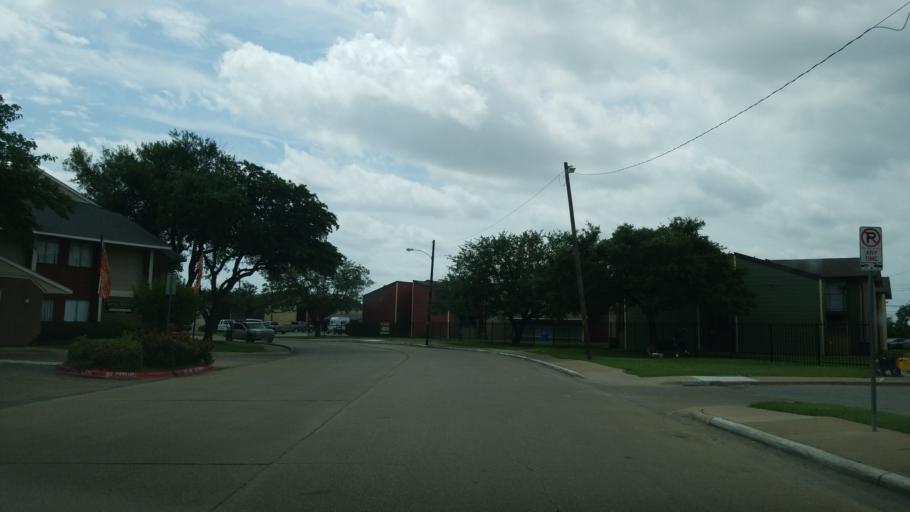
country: US
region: Texas
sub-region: Dallas County
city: Farmers Branch
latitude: 32.8749
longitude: -96.8705
